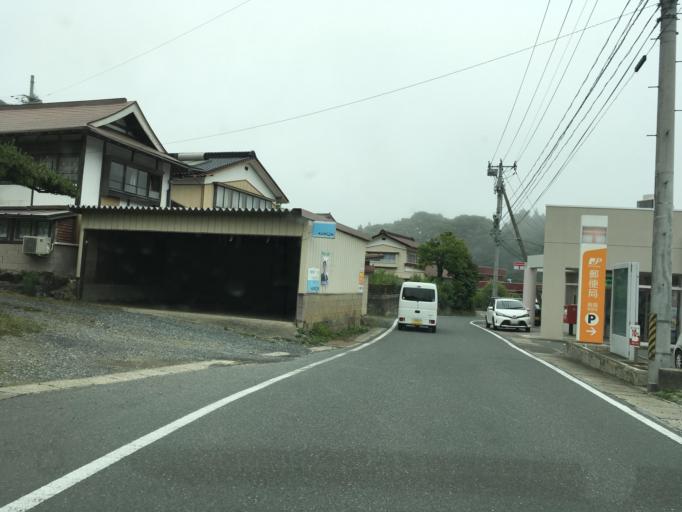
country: JP
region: Iwate
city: Ofunato
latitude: 38.9031
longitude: 141.6483
